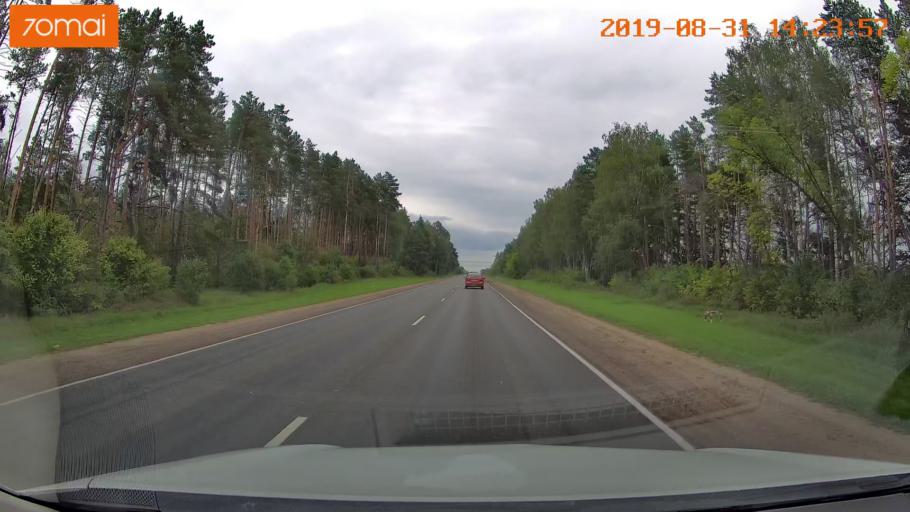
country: RU
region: Smolensk
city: Yekimovichi
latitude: 54.0999
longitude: 33.2452
